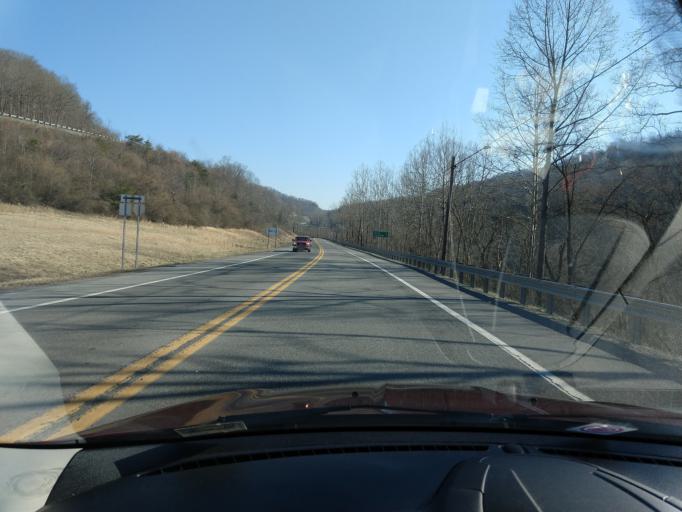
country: US
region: West Virginia
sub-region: Braxton County
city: Sutton
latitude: 38.6623
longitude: -80.7322
